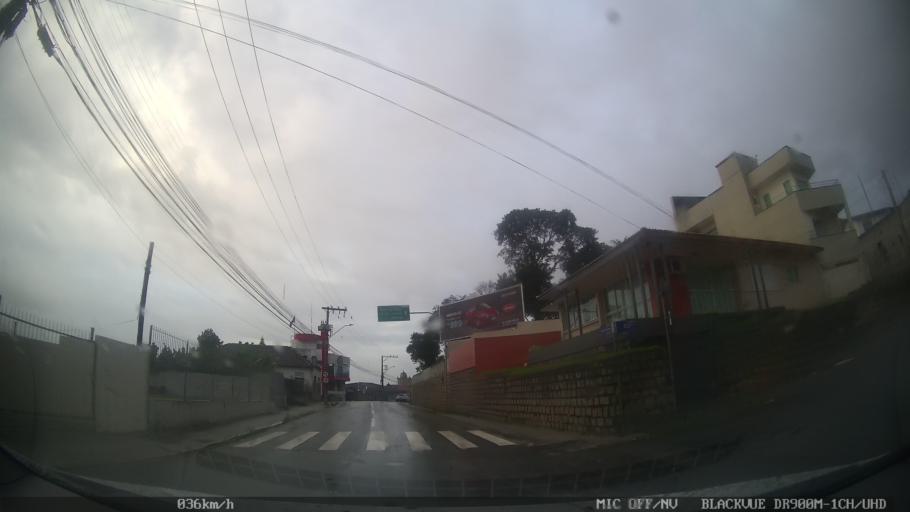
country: BR
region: Santa Catarina
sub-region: Sao Jose
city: Campinas
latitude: -27.6141
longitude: -48.6267
